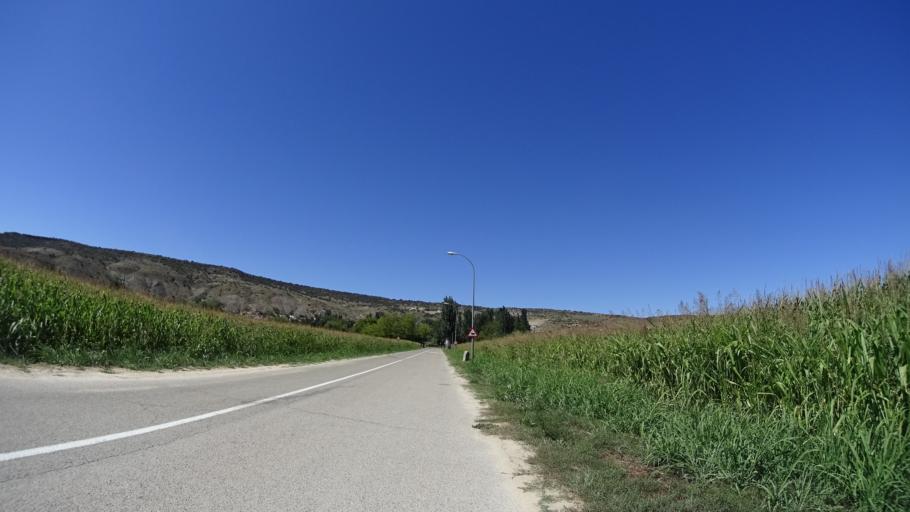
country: ES
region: Madrid
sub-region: Provincia de Madrid
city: Tielmes
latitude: 40.2394
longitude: -3.3115
